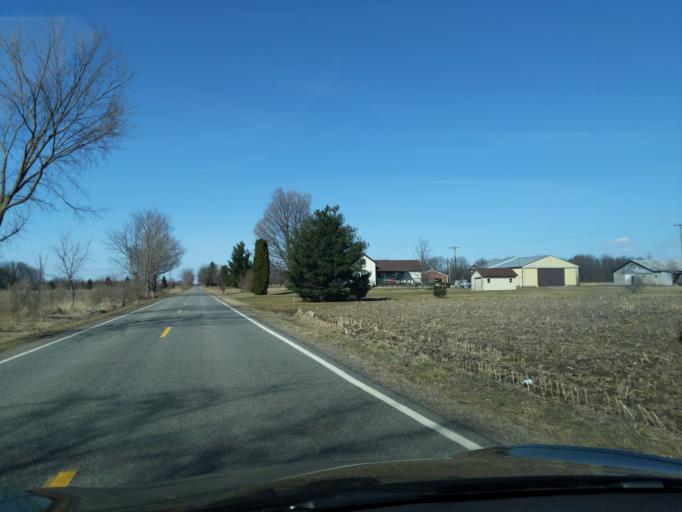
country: US
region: Michigan
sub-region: Ionia County
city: Saranac
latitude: 42.9189
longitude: -85.1341
